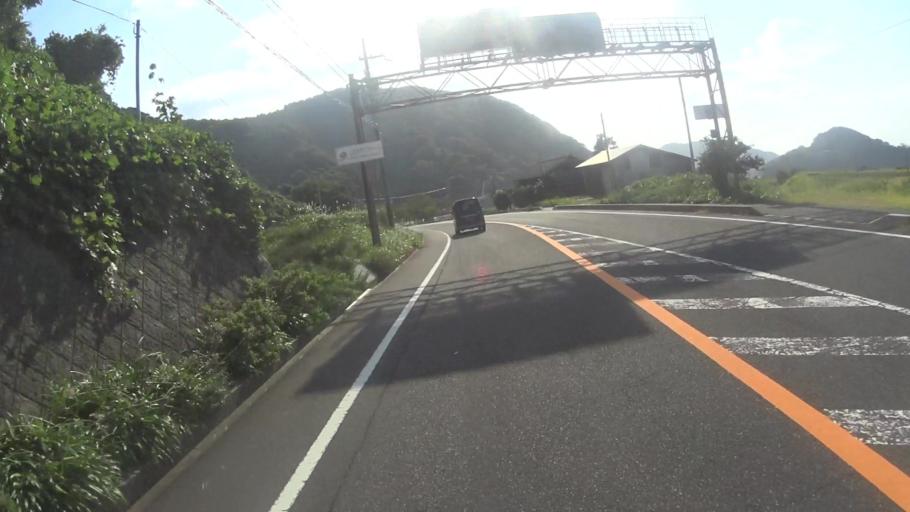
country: JP
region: Kyoto
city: Miyazu
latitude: 35.7431
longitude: 135.1185
